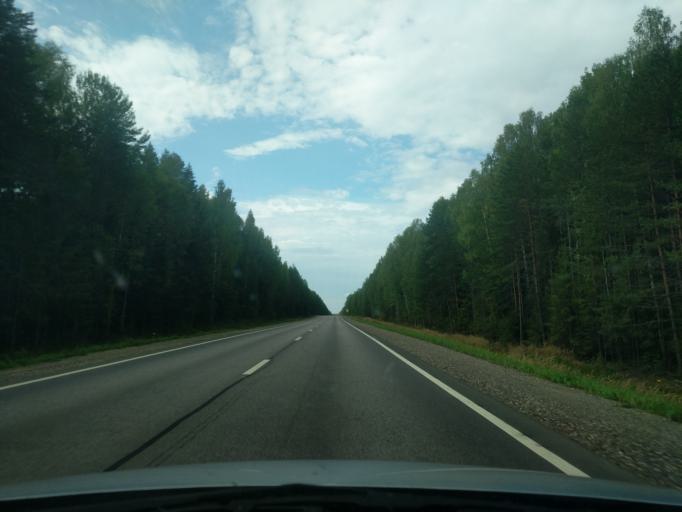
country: RU
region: Kostroma
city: Kadyy
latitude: 57.7960
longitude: 42.9243
